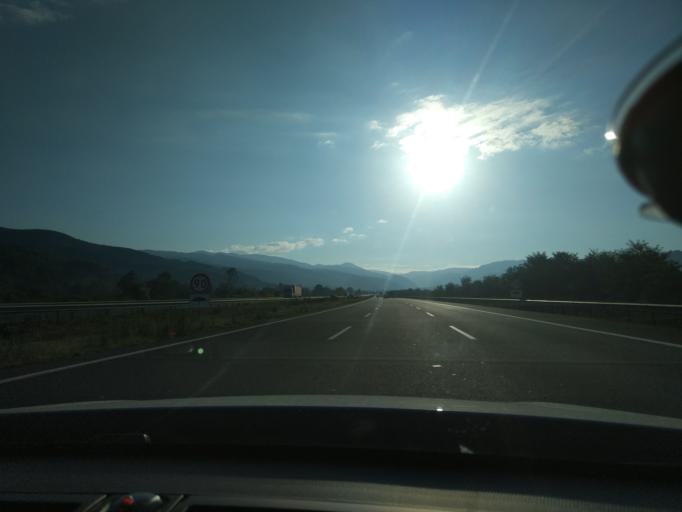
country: TR
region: Duzce
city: Kaynasli
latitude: 40.7842
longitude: 31.3027
